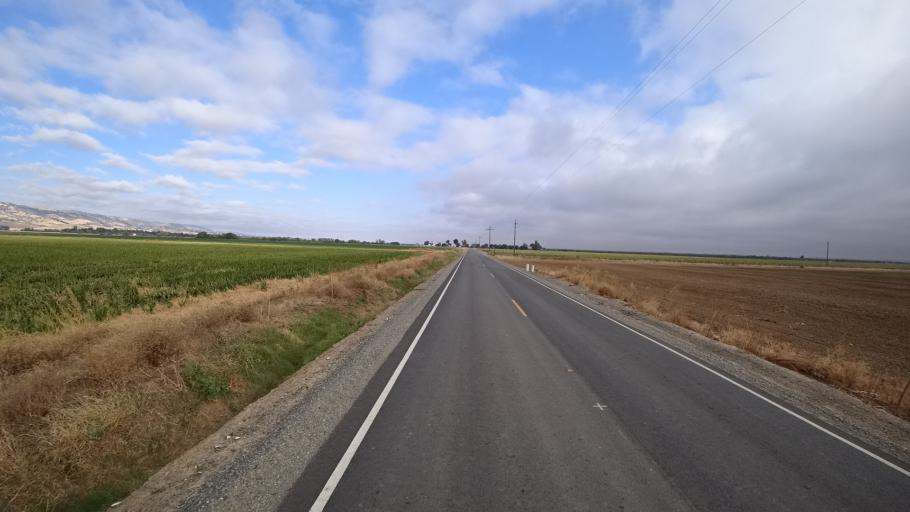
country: US
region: California
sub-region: Yolo County
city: Esparto
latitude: 38.7511
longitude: -122.0445
